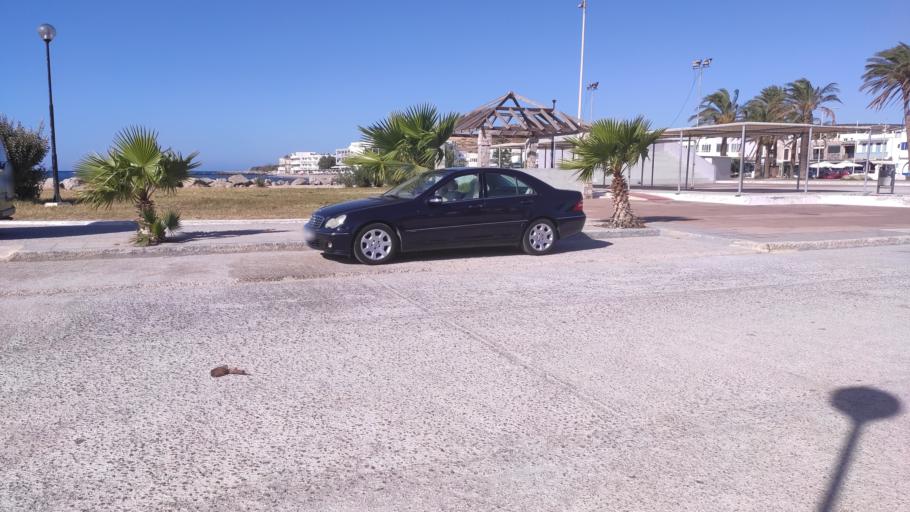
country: GR
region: South Aegean
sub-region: Nomos Dodekanisou
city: Kardamaina
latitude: 36.7810
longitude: 27.1443
